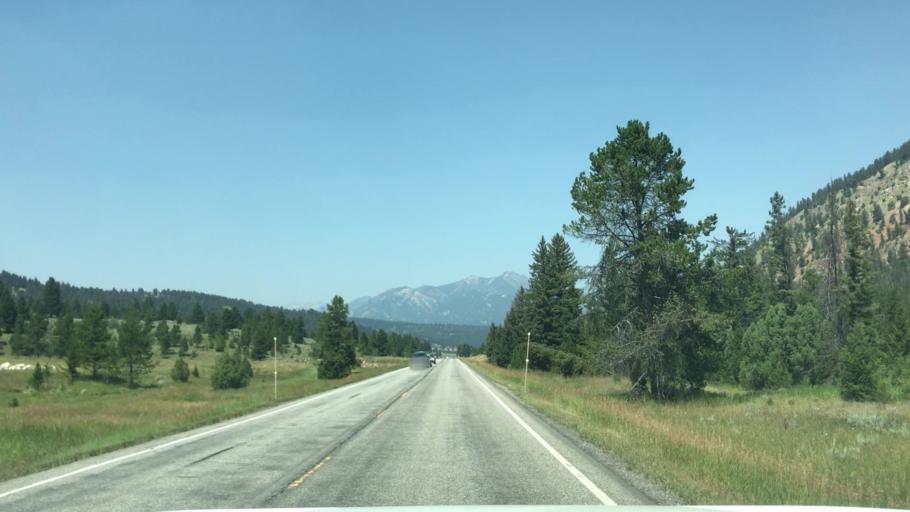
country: US
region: Montana
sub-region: Gallatin County
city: Big Sky
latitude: 45.2022
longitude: -111.2402
